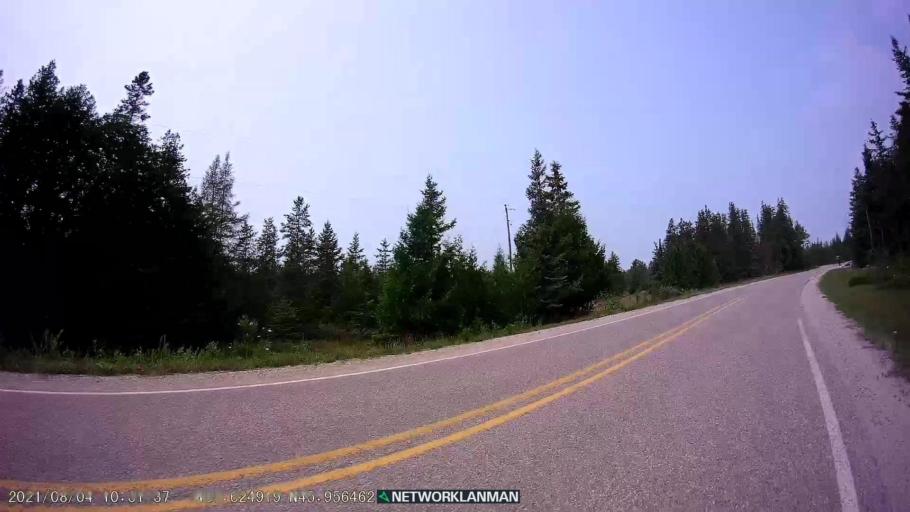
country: CA
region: Ontario
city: Thessalon
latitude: 45.9568
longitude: -83.6252
